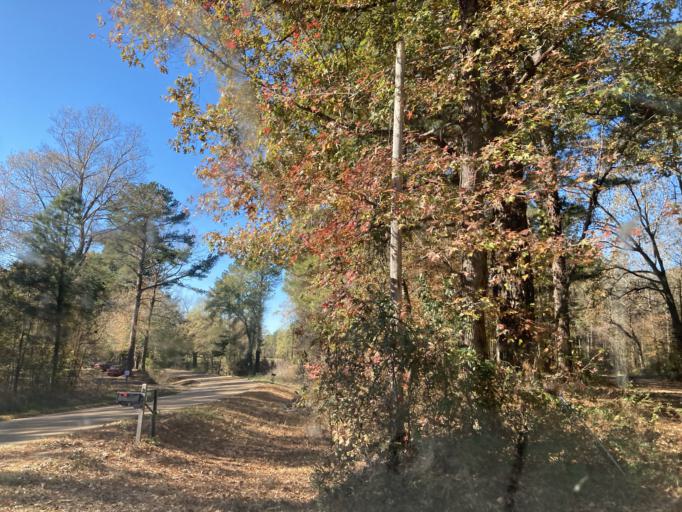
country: US
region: Mississippi
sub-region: Hinds County
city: Lynchburg
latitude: 32.5956
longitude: -90.5410
